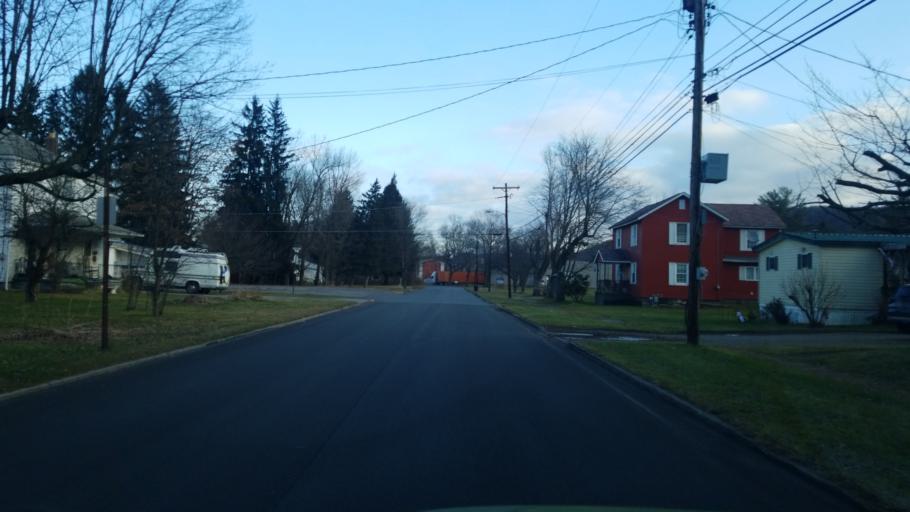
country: US
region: Pennsylvania
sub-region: Clearfield County
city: Clearfield
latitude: 41.0103
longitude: -78.4438
